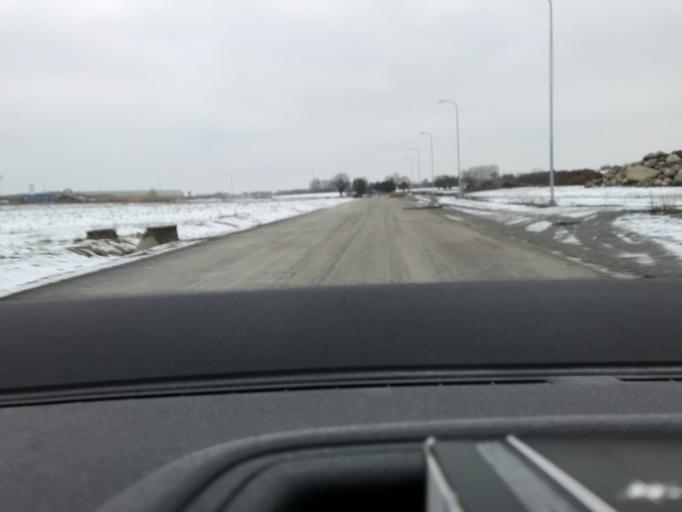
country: SE
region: Skane
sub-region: Ystads Kommun
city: Ystad
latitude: 55.4477
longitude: 13.8549
